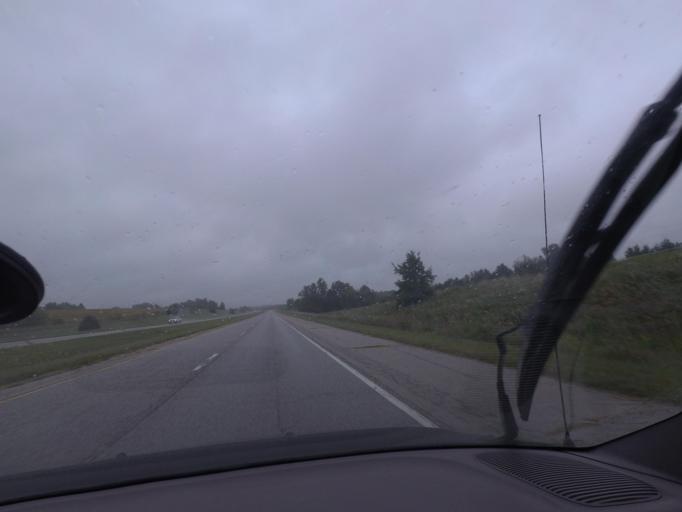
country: US
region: Illinois
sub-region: Pike County
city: Pittsfield
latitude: 39.6797
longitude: -90.8699
